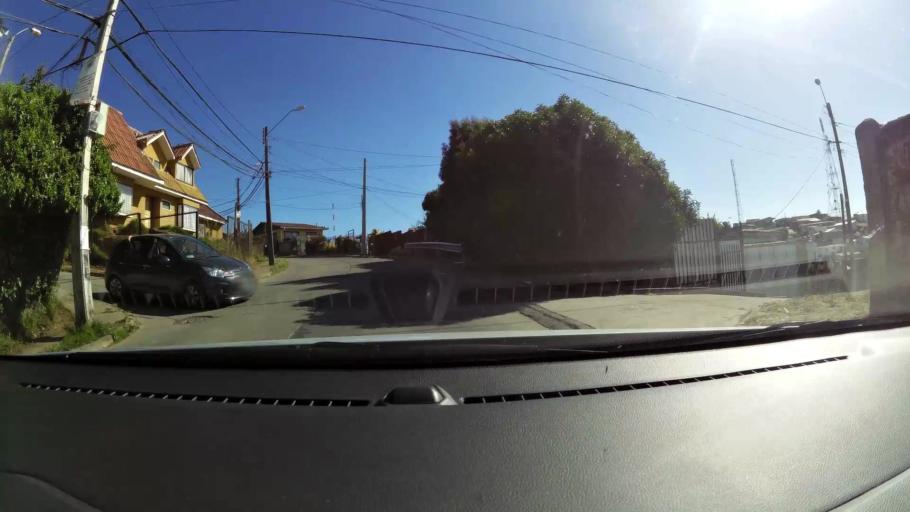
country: CL
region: Valparaiso
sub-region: Provincia de Valparaiso
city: Vina del Mar
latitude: -33.0441
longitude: -71.5631
